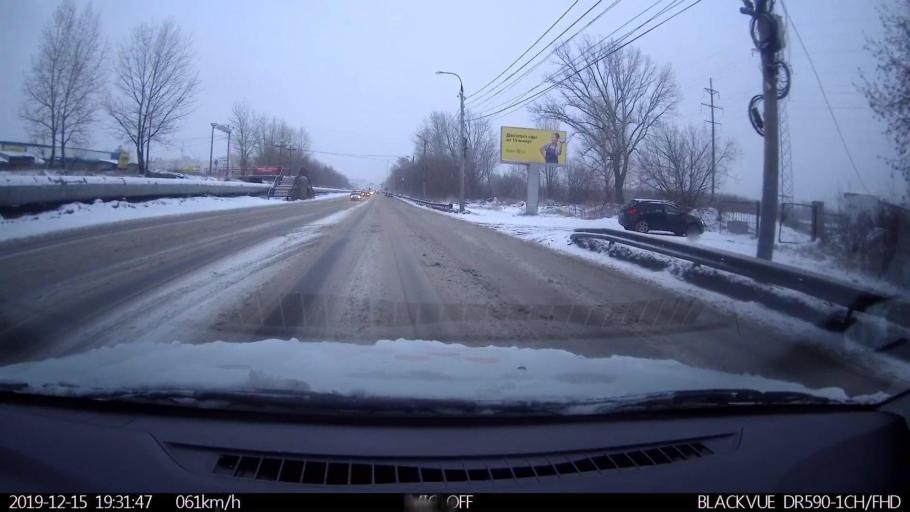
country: RU
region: Nizjnij Novgorod
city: Nizhniy Novgorod
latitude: 56.3432
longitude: 43.8981
